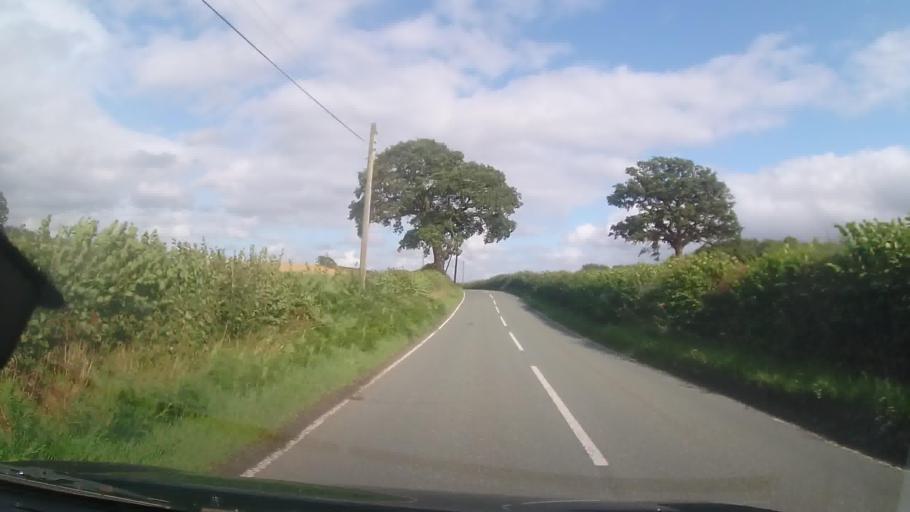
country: GB
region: England
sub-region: Shropshire
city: Lydham
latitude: 52.4985
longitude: -2.9824
